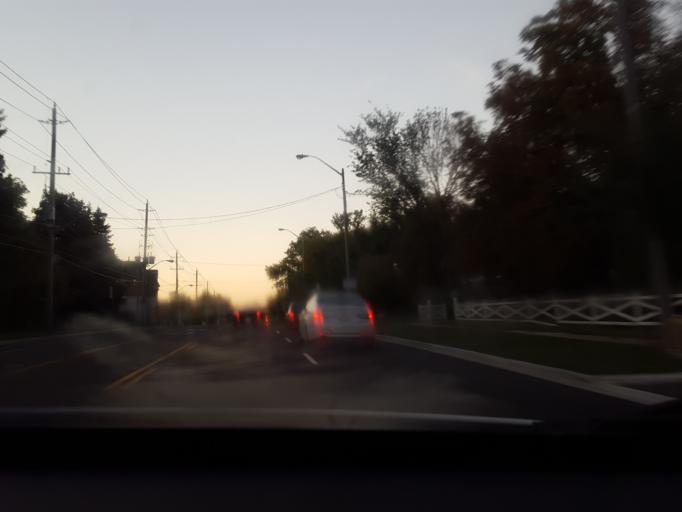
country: CA
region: Ontario
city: Willowdale
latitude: 43.7450
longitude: -79.3835
